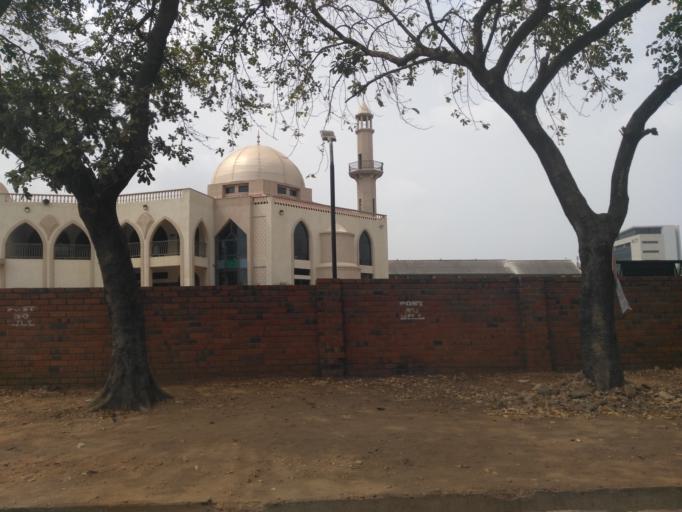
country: GH
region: Greater Accra
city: Accra
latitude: 5.5716
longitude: -0.1802
